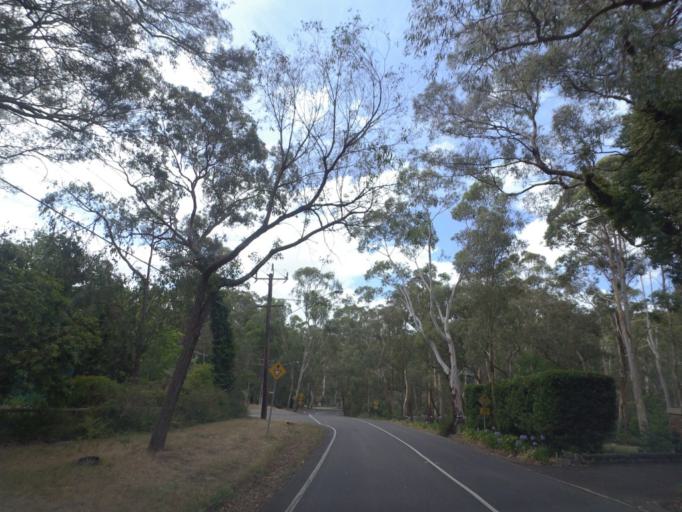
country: AU
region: Victoria
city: Mitcham
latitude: -37.7962
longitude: 145.2027
